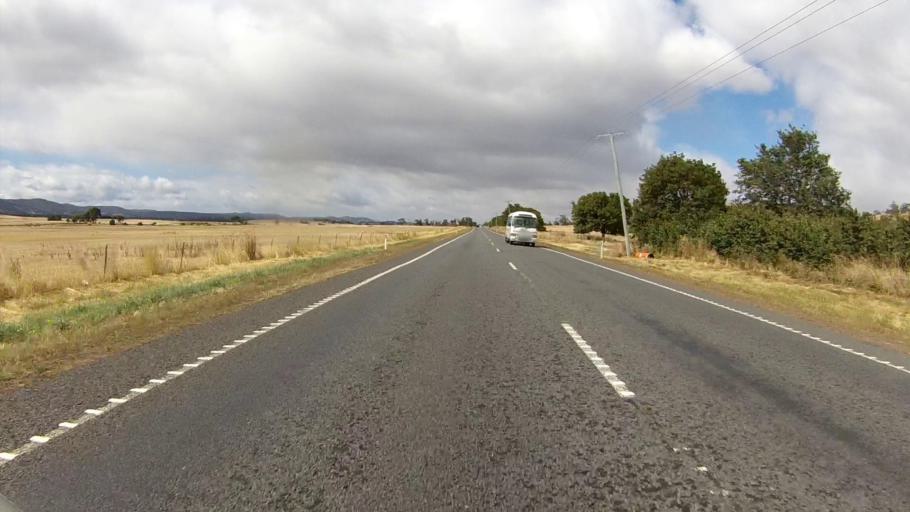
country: AU
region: Tasmania
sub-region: Northern Midlands
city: Evandale
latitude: -41.9677
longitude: 147.5007
